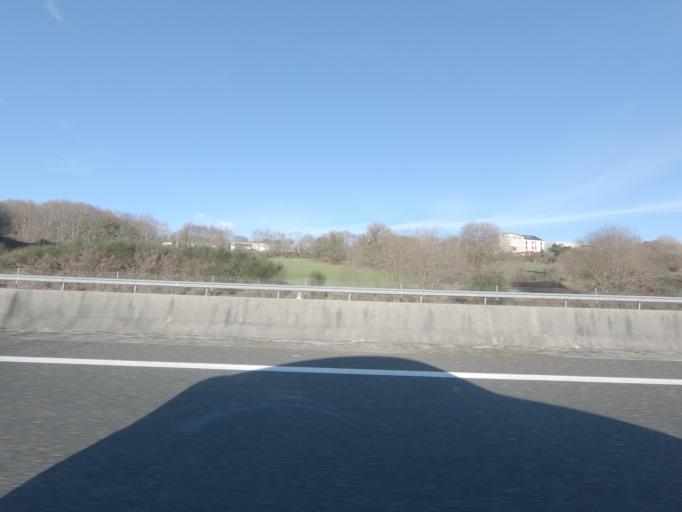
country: ES
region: Galicia
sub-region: Provincia de Pontevedra
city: Lalin
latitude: 42.6681
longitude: -8.1488
